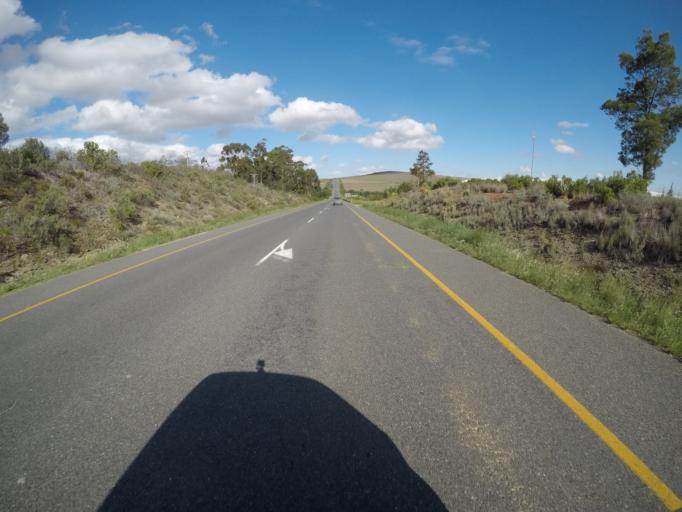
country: ZA
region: Western Cape
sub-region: Overberg District Municipality
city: Swellendam
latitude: -33.9615
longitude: 20.2415
